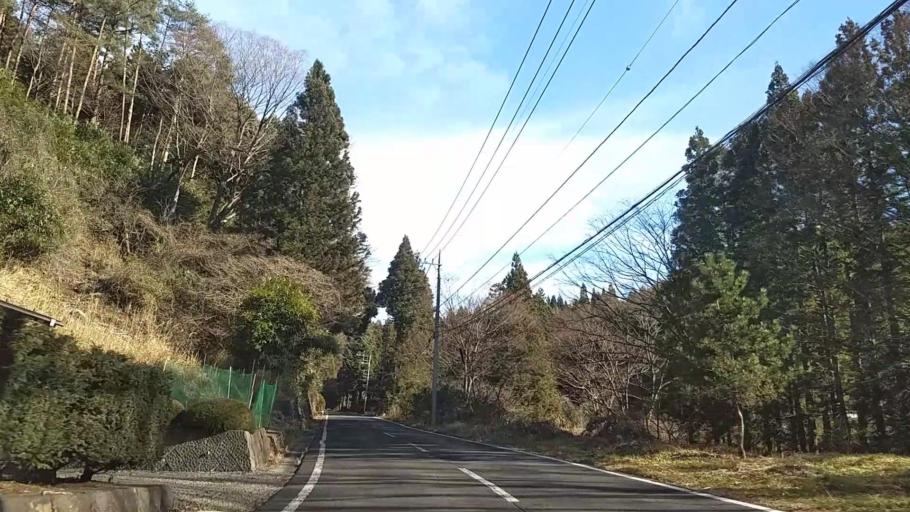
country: JP
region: Yamanashi
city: Otsuki
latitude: 35.5180
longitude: 138.9333
